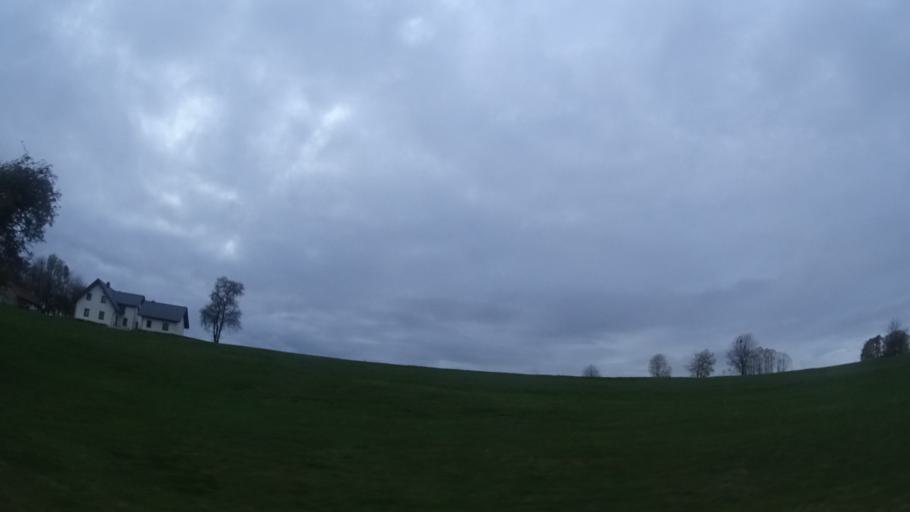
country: DE
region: Hesse
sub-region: Regierungsbezirk Giessen
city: Freiensteinau
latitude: 50.3821
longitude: 9.4362
